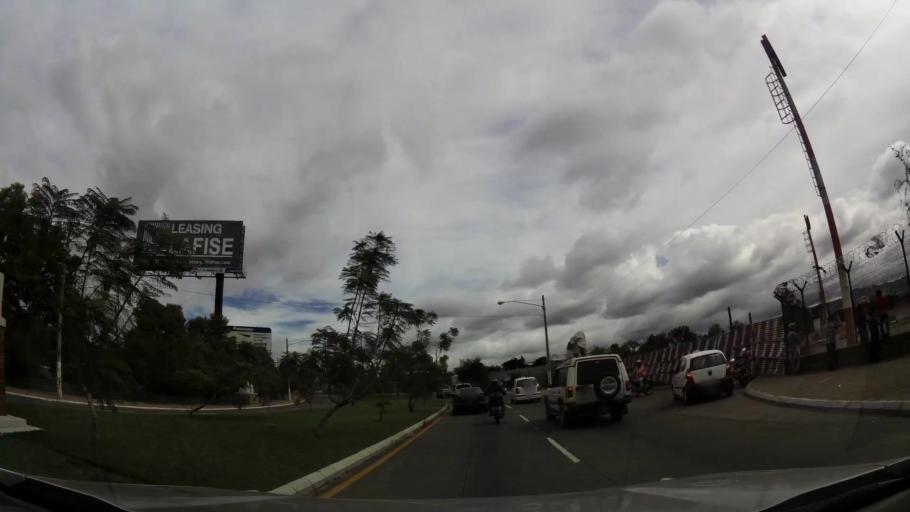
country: GT
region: Guatemala
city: Santa Catarina Pinula
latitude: 14.5936
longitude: -90.5283
